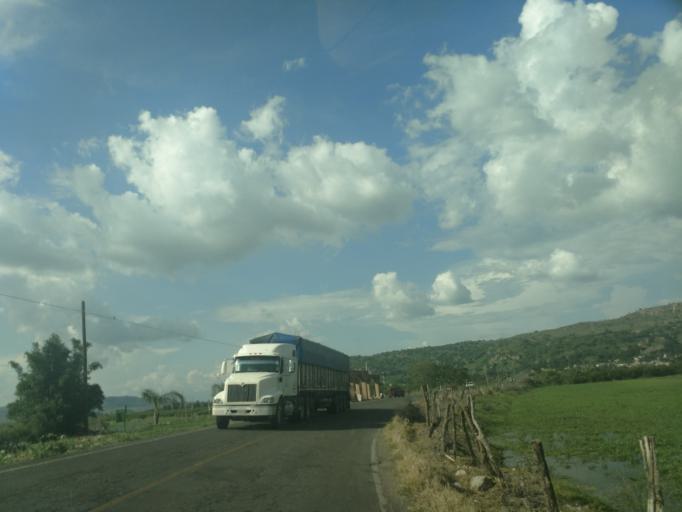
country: MX
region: Jalisco
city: Antonio Escobedo
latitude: 20.9033
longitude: -103.9949
